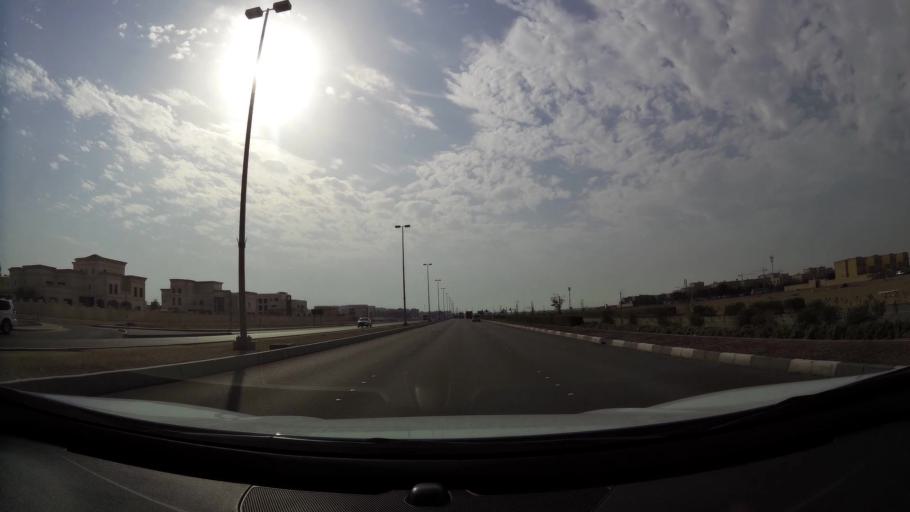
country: AE
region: Abu Dhabi
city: Abu Dhabi
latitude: 24.3477
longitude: 54.5484
